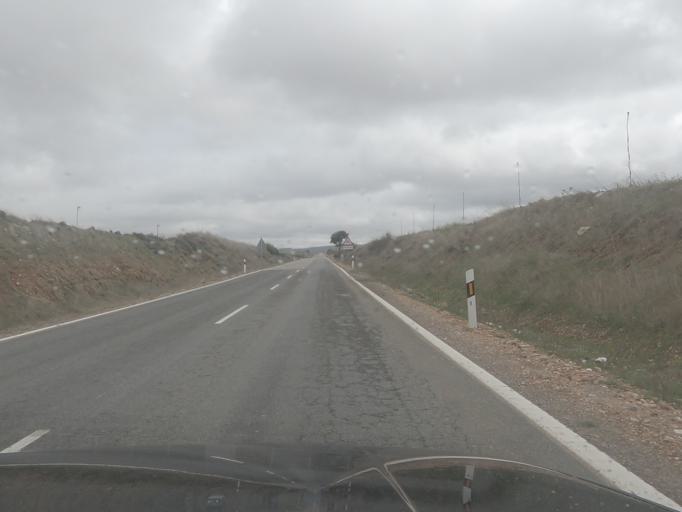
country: ES
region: Castille and Leon
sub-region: Provincia de Zamora
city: Pozuelo de Tabara
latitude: 41.7789
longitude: -5.8865
